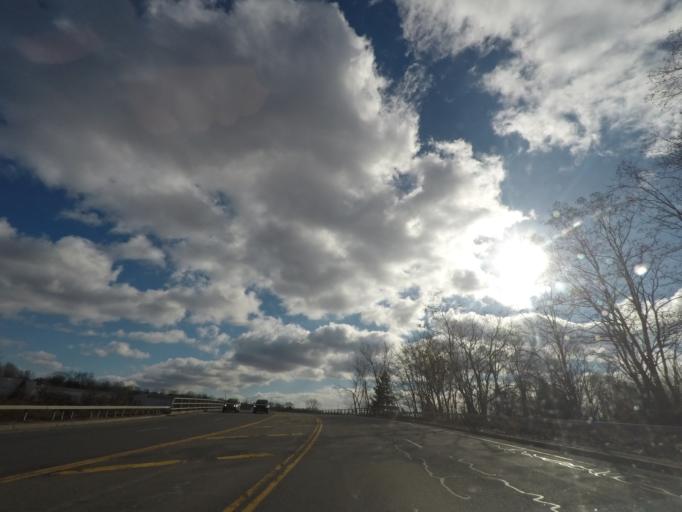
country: US
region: New York
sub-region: Schenectady County
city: Schenectady
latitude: 42.8309
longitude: -73.9313
